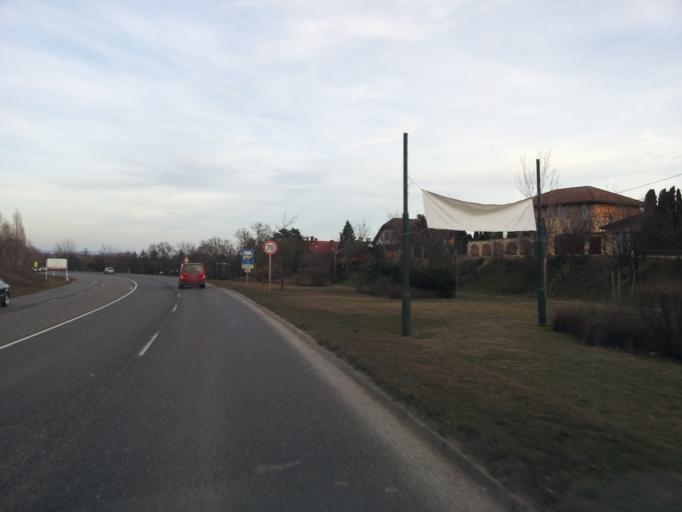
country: HU
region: Veszprem
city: Csopak
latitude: 46.9619
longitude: 17.9013
